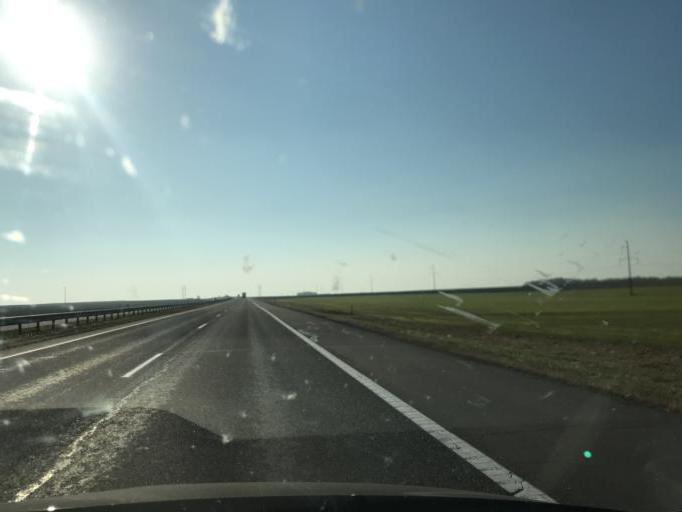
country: BY
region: Minsk
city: Snow
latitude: 53.3305
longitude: 26.4223
